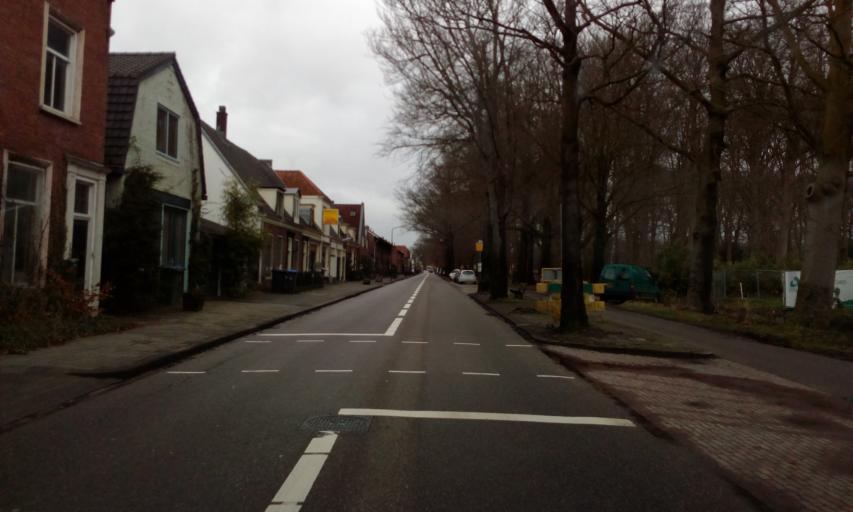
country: NL
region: North Holland
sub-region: Gemeente Wijdemeren
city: Kortenhoef
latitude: 52.2448
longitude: 5.1214
